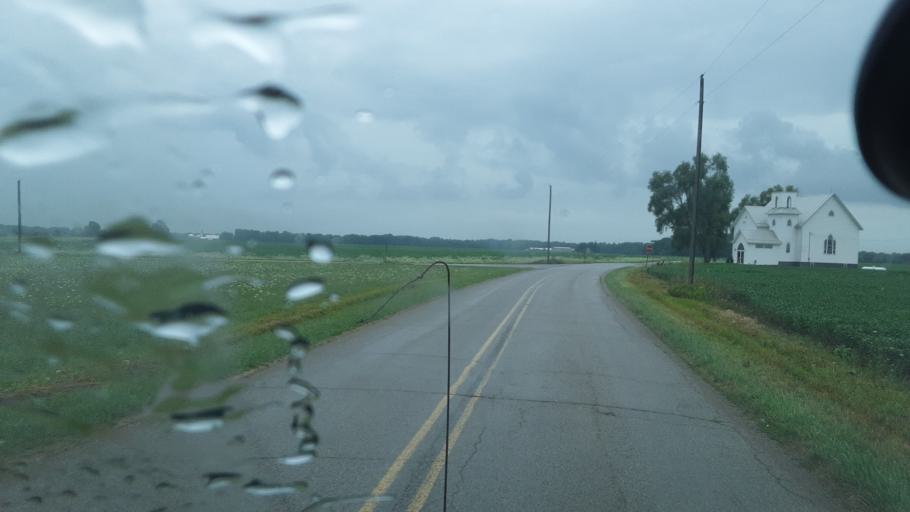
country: US
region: Ohio
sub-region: Williams County
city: Edgerton
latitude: 41.5034
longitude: -84.8139
